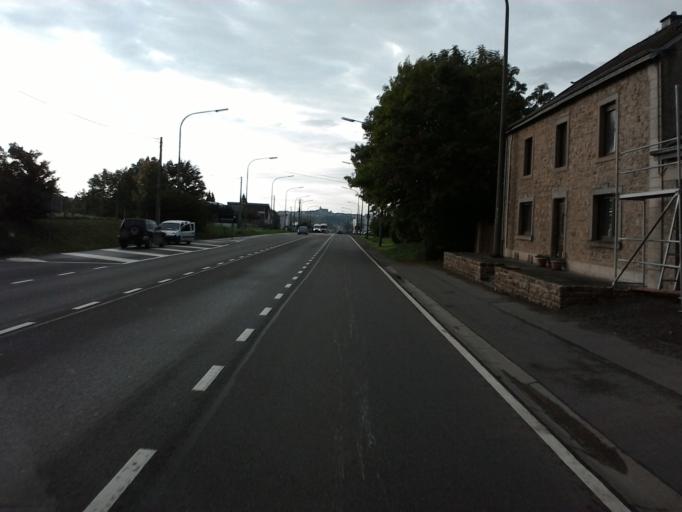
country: BE
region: Wallonia
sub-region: Province du Luxembourg
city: Arlon
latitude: 49.7063
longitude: 5.8045
